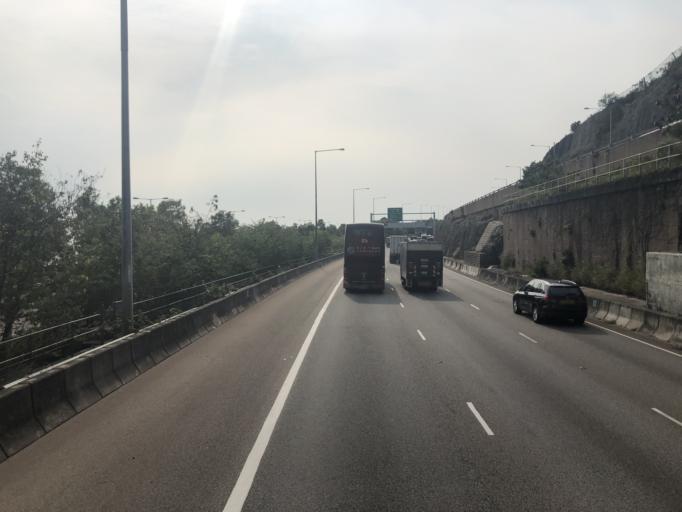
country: HK
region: Tuen Mun
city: Tuen Mun
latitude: 22.3559
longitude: 114.0250
